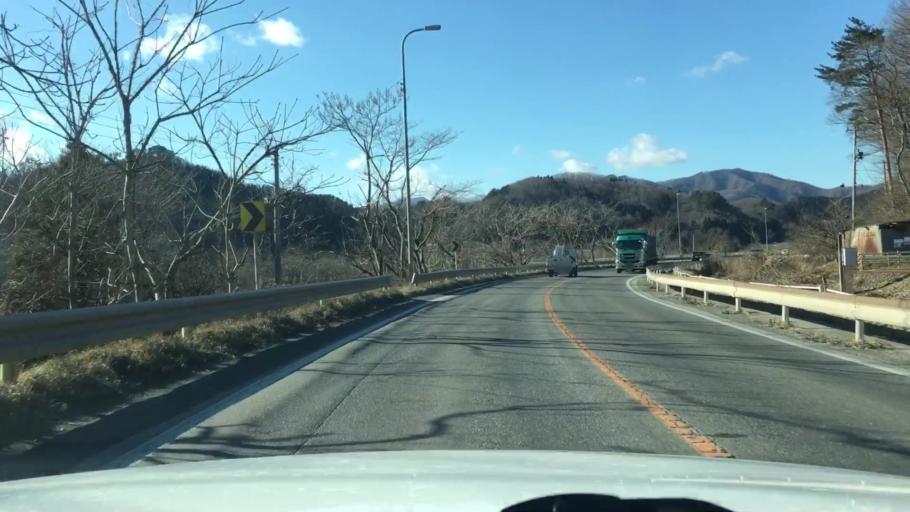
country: JP
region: Iwate
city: Miyako
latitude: 39.6289
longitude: 141.8584
